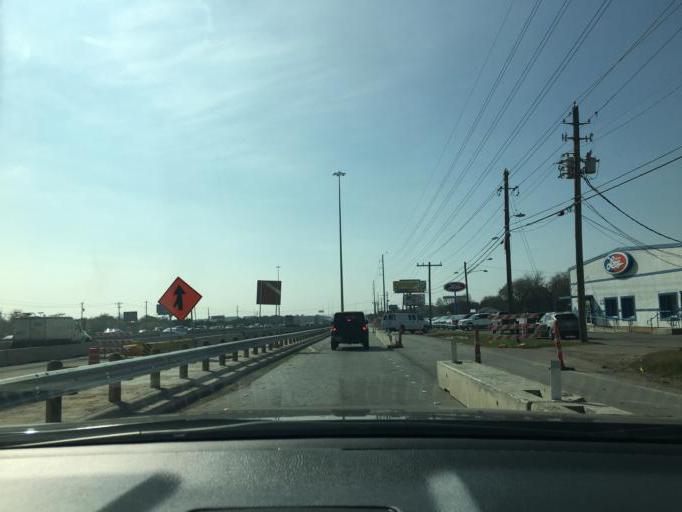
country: US
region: Texas
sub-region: Travis County
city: Onion Creek
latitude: 30.1877
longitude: -97.7729
